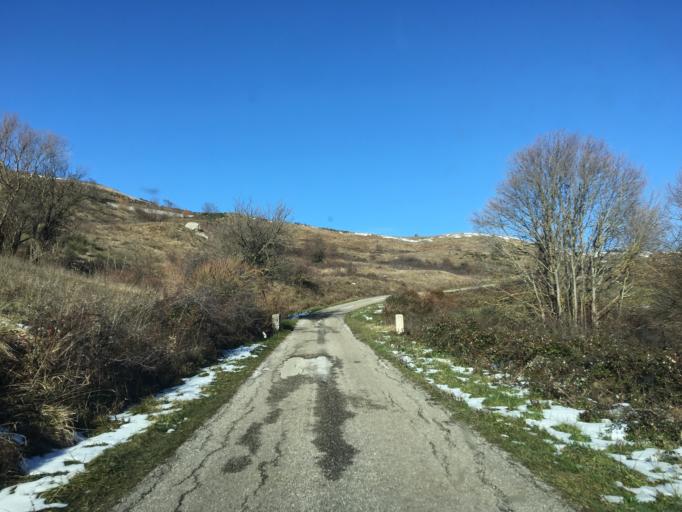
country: IT
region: Molise
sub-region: Provincia di Isernia
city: Agnone
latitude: 41.8502
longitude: 14.3541
